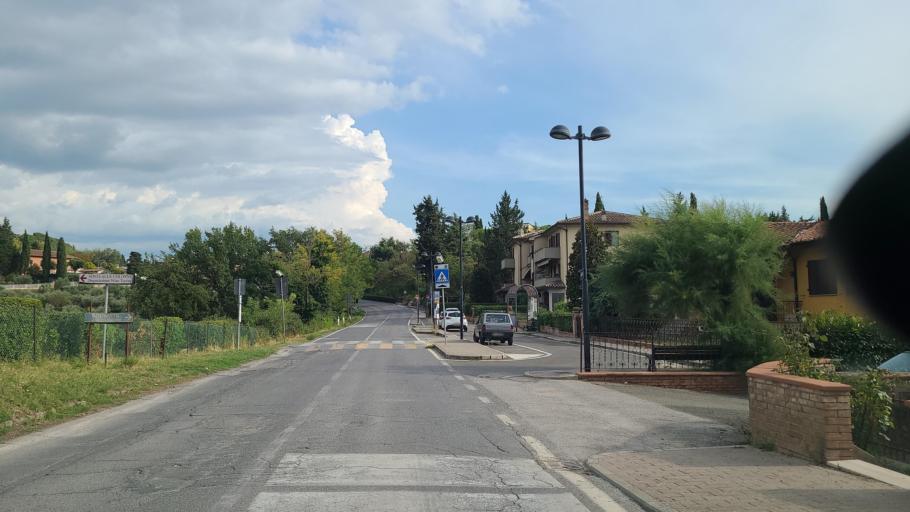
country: IT
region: Tuscany
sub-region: Provincia di Siena
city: San Gimignano
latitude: 43.4731
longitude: 11.0319
